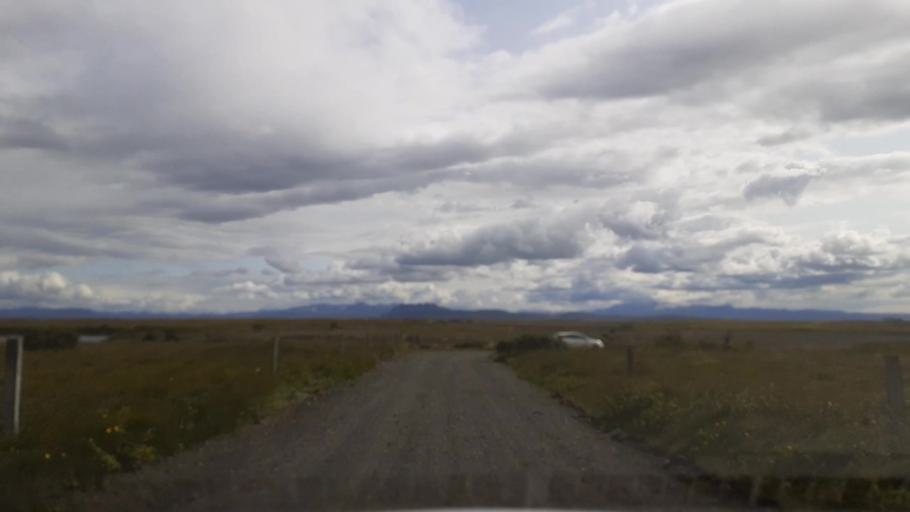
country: IS
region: South
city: Vestmannaeyjar
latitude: 63.8189
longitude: -20.4206
